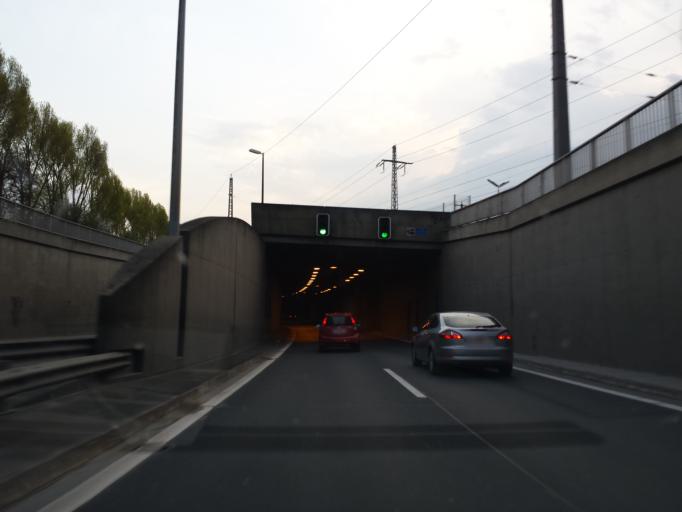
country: AT
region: Lower Austria
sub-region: Politischer Bezirk Wien-Umgebung
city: Gerasdorf bei Wien
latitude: 48.2349
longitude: 16.4557
